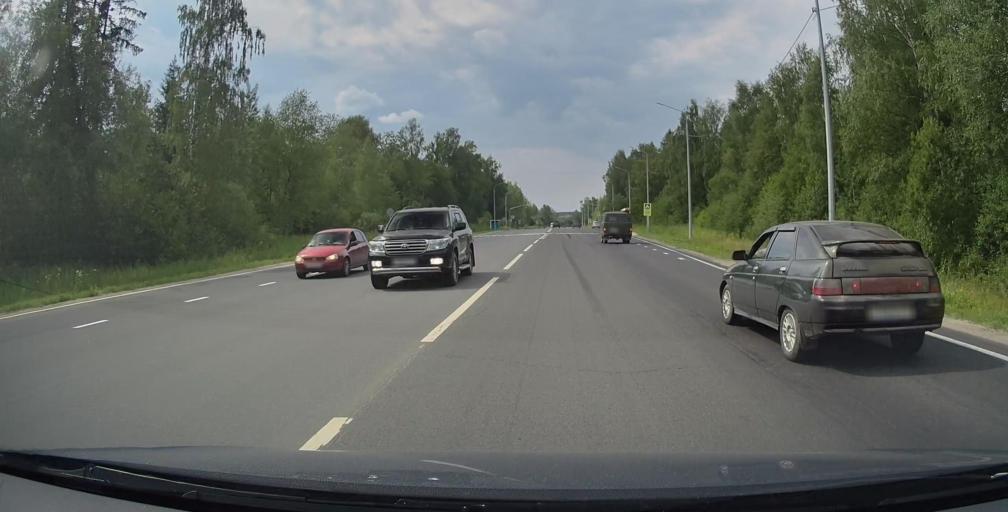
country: RU
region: Jaroslavl
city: Tutayev
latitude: 57.8836
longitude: 39.4500
